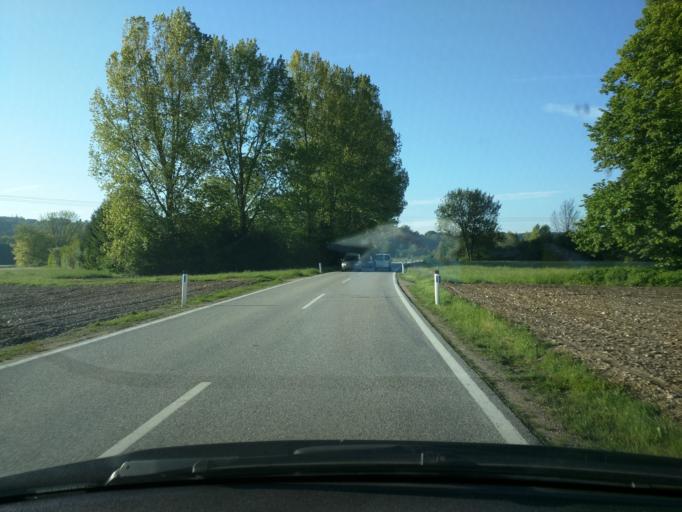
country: AT
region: Lower Austria
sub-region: Politischer Bezirk Melk
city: Blindenmarkt
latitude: 48.1240
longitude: 15.0133
